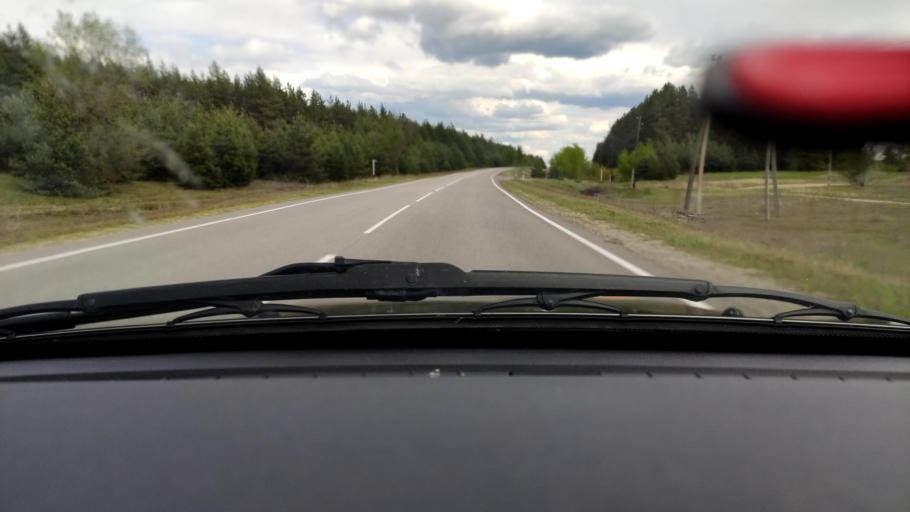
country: RU
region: Voronezj
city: Uryv-Pokrovka
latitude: 51.0547
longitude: 38.9555
